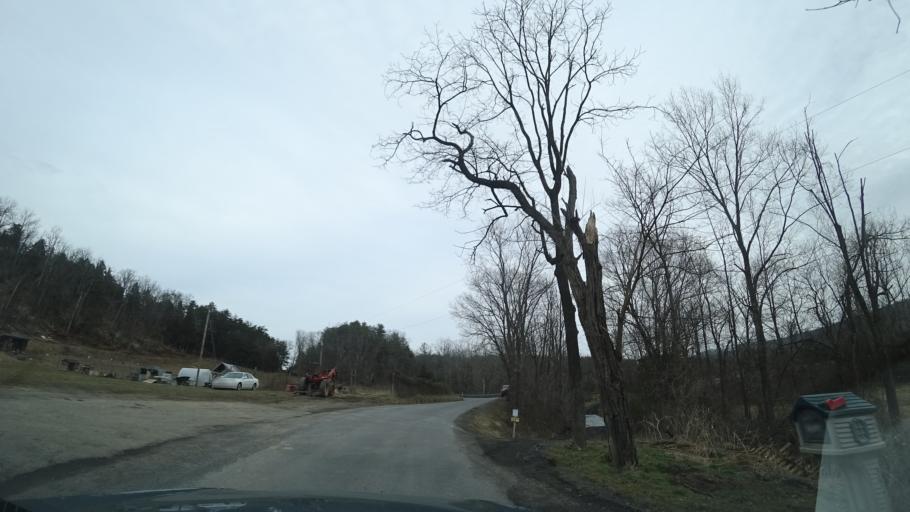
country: US
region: Virginia
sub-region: Shenandoah County
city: Woodstock
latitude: 39.0712
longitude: -78.6270
